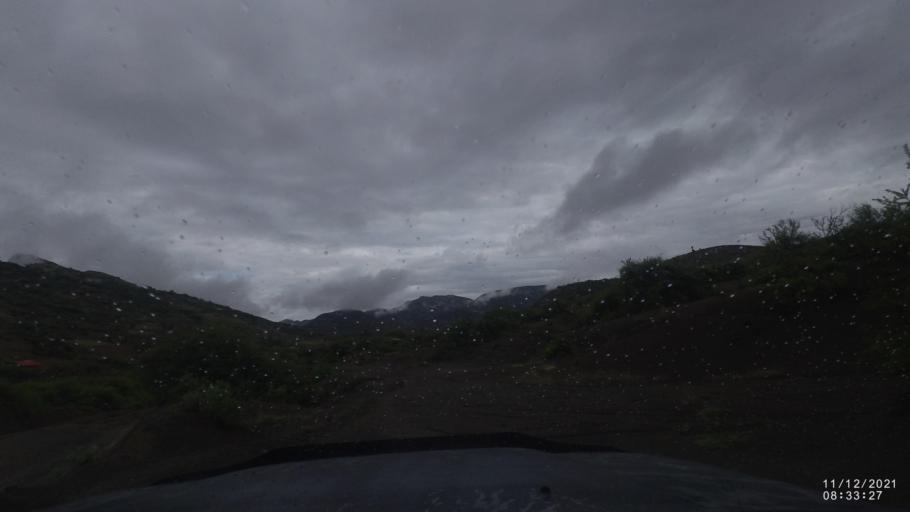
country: BO
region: Cochabamba
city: Tarata
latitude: -17.9352
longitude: -65.9338
